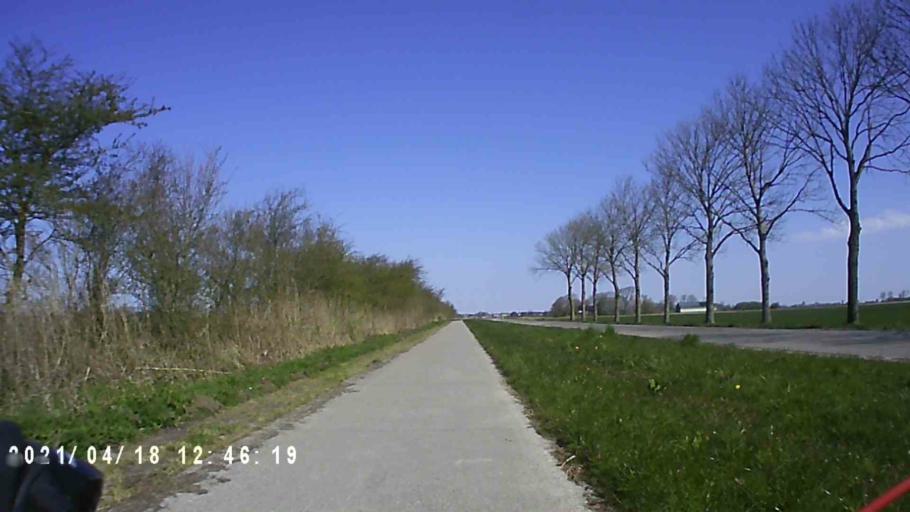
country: NL
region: Friesland
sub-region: Gemeente Dongeradeel
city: Dokkum
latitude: 53.3654
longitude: 6.0481
